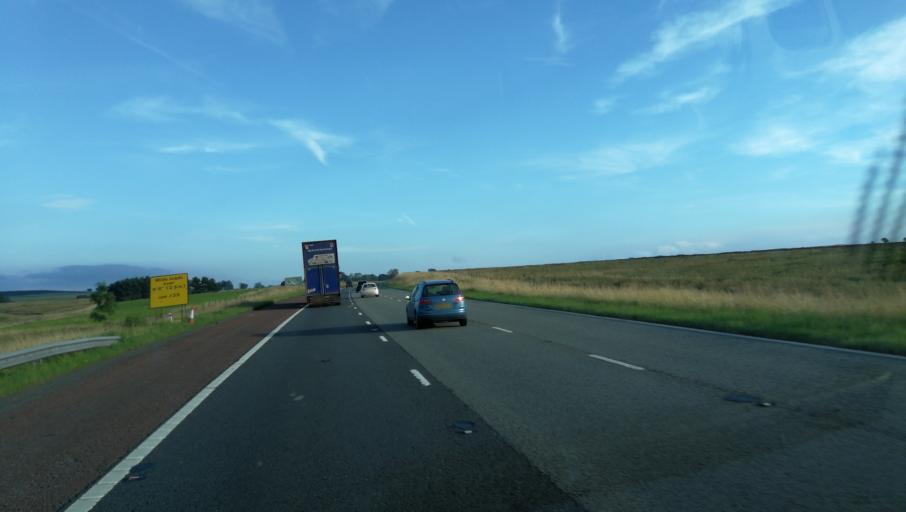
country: GB
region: England
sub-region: Cumbria
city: Penrith
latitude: 54.5479
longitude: -2.6651
